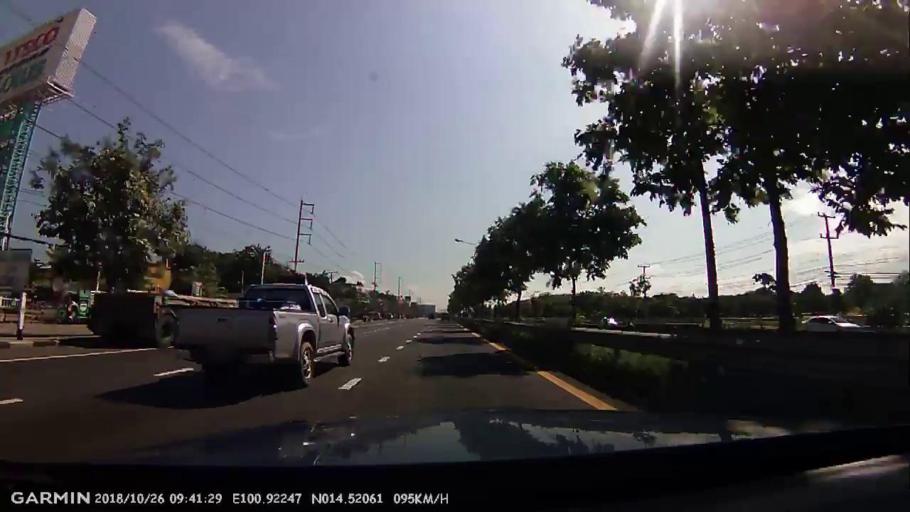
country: TH
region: Sara Buri
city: Saraburi
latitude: 14.5206
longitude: 100.9227
